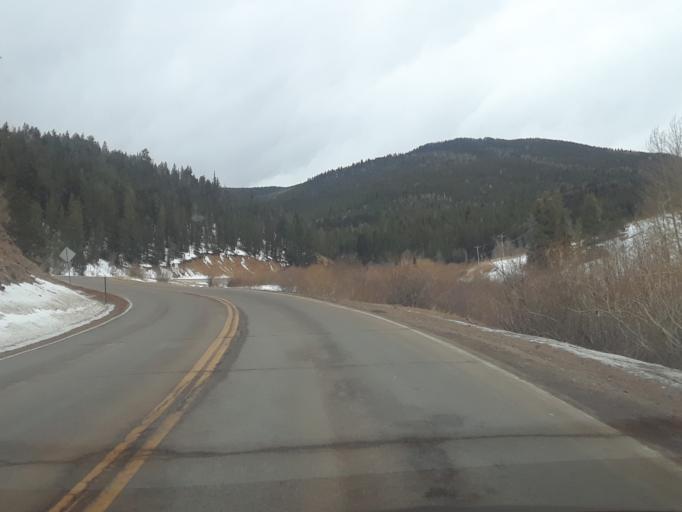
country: US
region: Colorado
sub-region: Boulder County
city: Coal Creek
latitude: 39.8293
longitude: -105.4104
